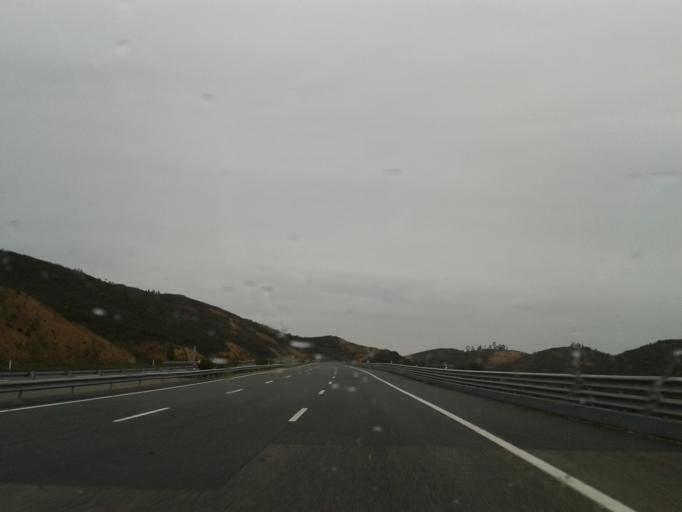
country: PT
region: Faro
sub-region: Silves
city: Sao Bartolomeu de Messines
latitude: 37.3292
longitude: -8.2595
